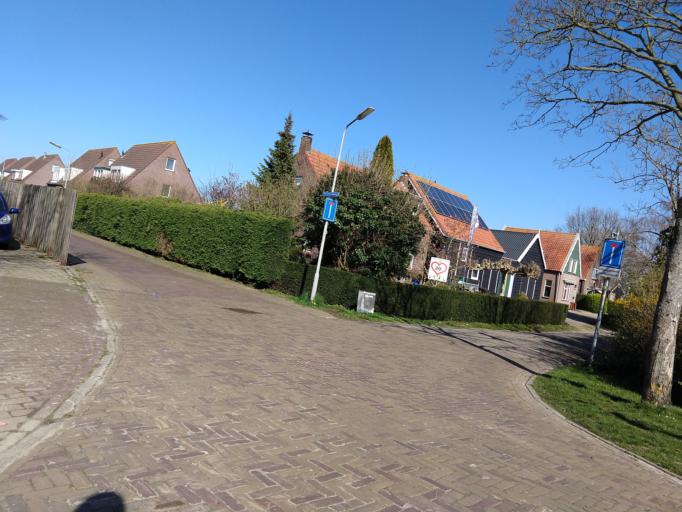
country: NL
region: Zeeland
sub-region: Gemeente Goes
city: Goes
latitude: 51.5229
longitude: 3.9455
